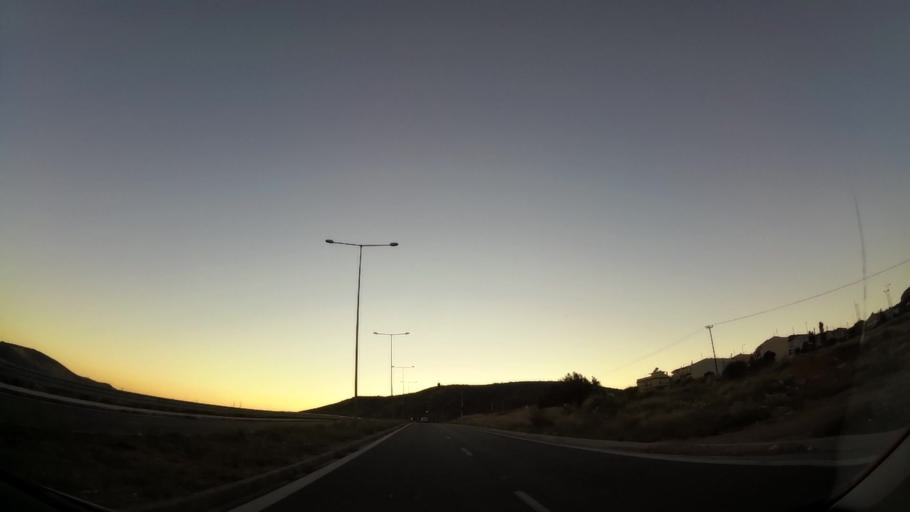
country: GR
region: Attica
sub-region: Nomarchia Dytikis Attikis
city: Ano Liosia
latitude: 38.0963
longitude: 23.6942
